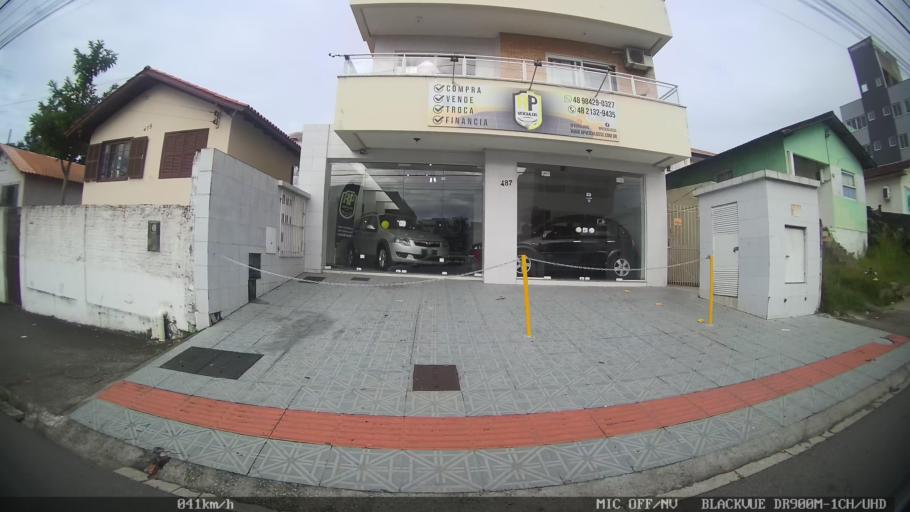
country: BR
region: Santa Catarina
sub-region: Sao Jose
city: Campinas
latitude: -27.5706
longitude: -48.6176
